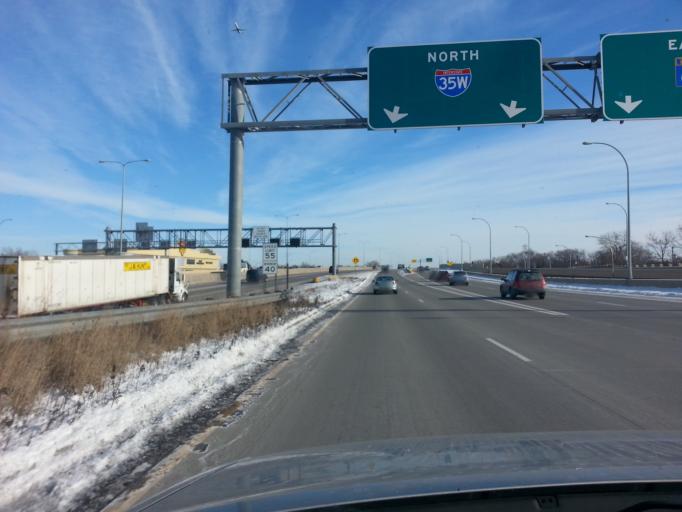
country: US
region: Minnesota
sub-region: Hennepin County
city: Richfield
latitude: 44.8898
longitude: -93.2917
